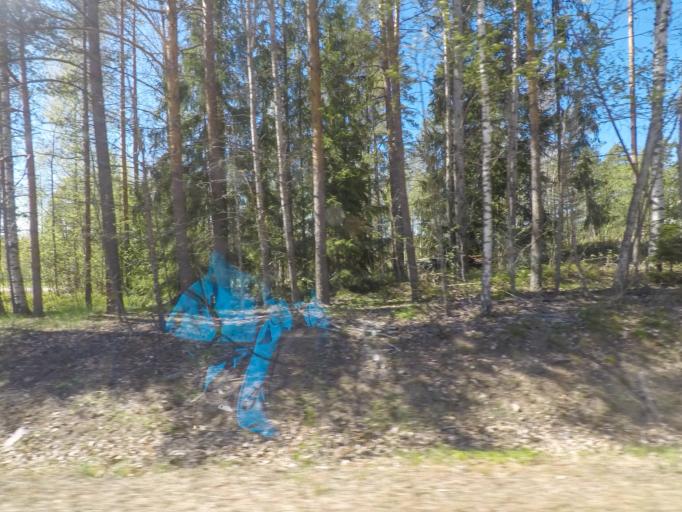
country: FI
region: Uusimaa
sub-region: Helsinki
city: Sammatti
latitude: 60.3533
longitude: 23.8007
